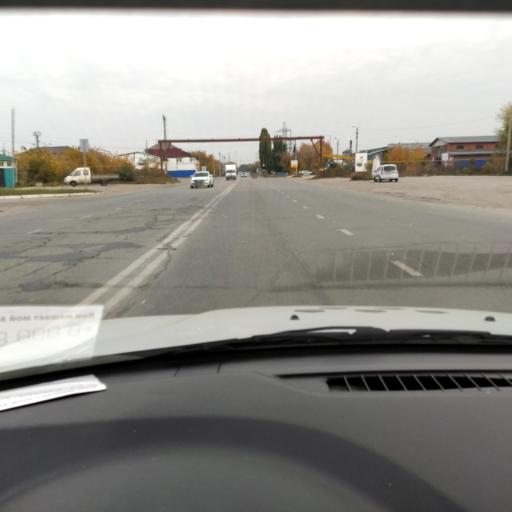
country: RU
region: Samara
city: Tol'yatti
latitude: 53.5230
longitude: 49.4701
